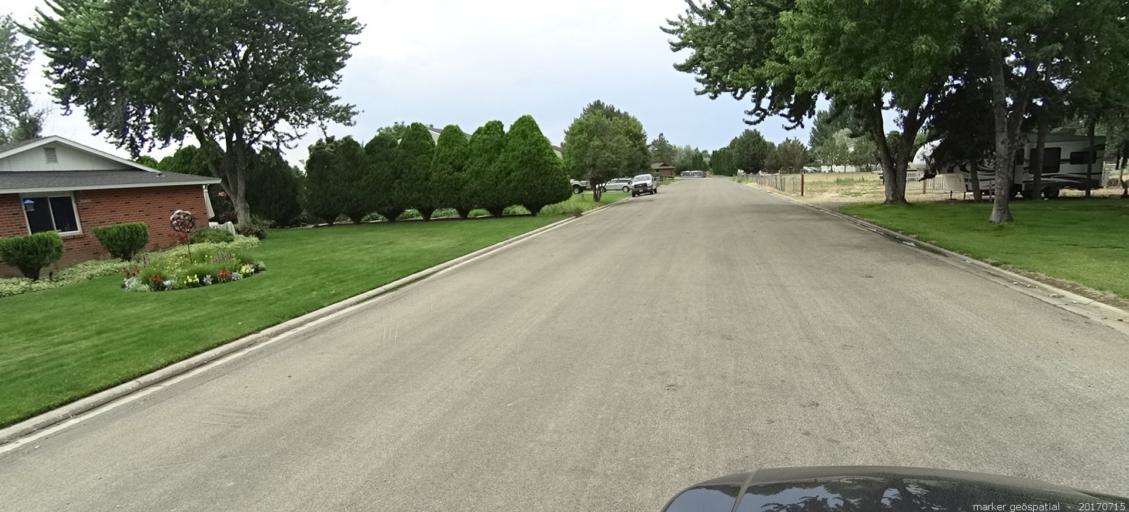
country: US
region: Idaho
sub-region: Ada County
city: Garden City
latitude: 43.5538
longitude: -116.3010
